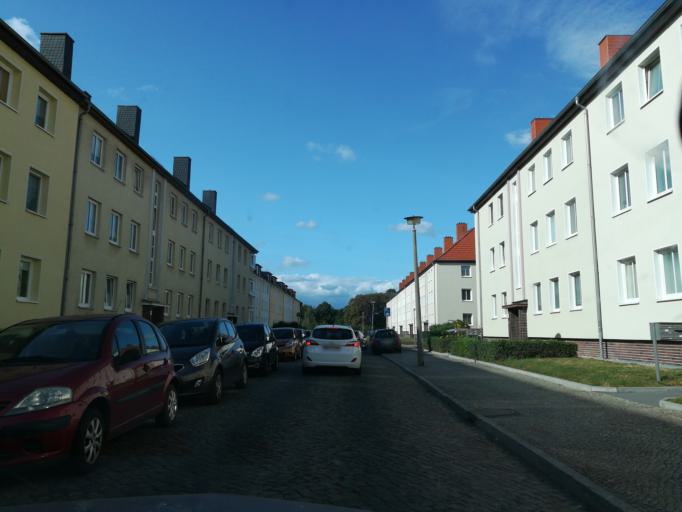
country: DE
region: Saxony-Anhalt
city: Magdeburg
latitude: 52.1300
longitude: 11.5979
